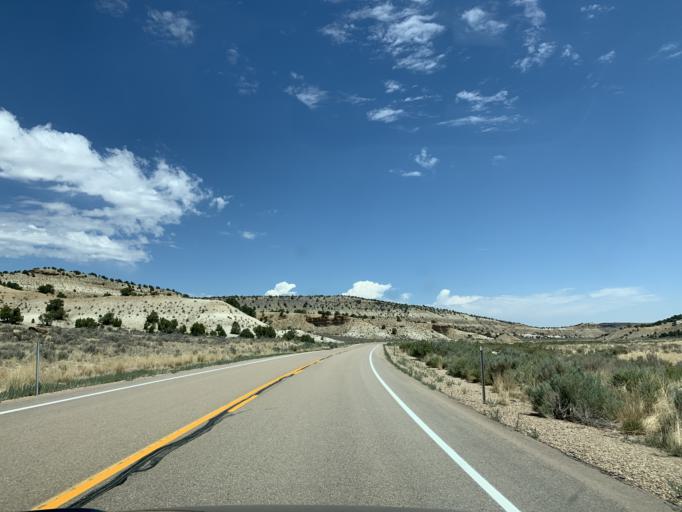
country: US
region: Utah
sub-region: Duchesne County
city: Duchesne
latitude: 39.9601
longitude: -110.1875
